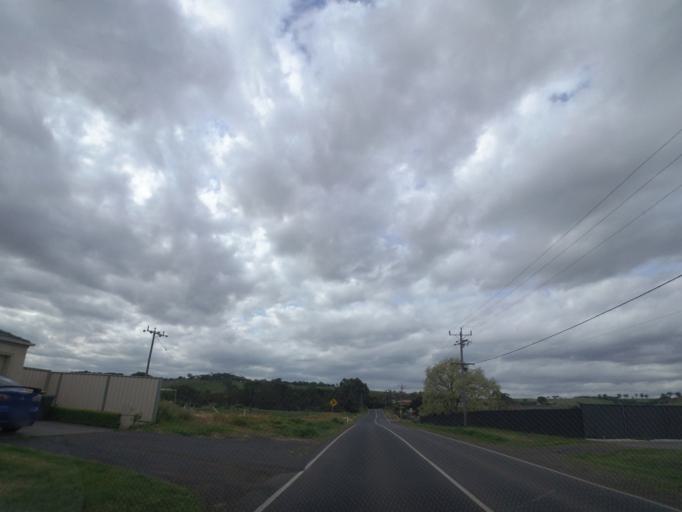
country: AU
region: Victoria
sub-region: Brimbank
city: Keilor
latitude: -37.7083
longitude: 144.8320
